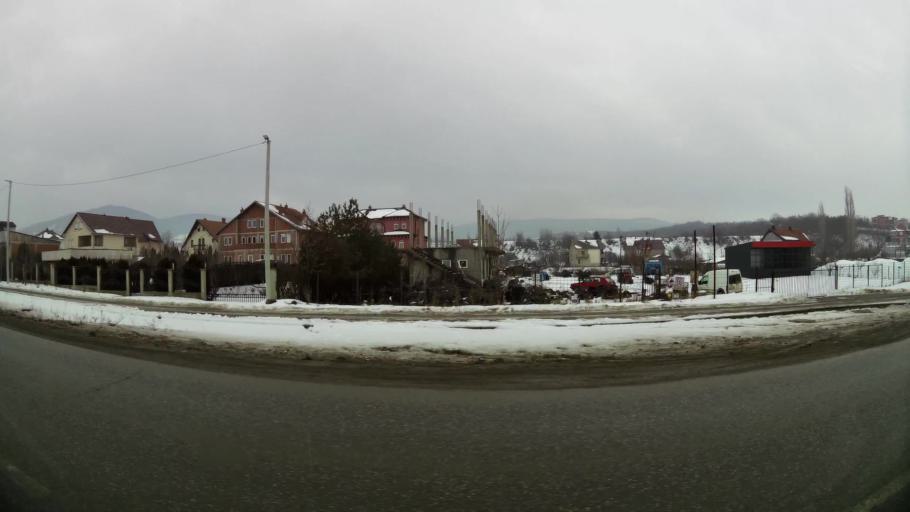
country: XK
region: Pristina
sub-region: Komuna e Prishtines
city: Pristina
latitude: 42.7085
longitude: 21.1536
